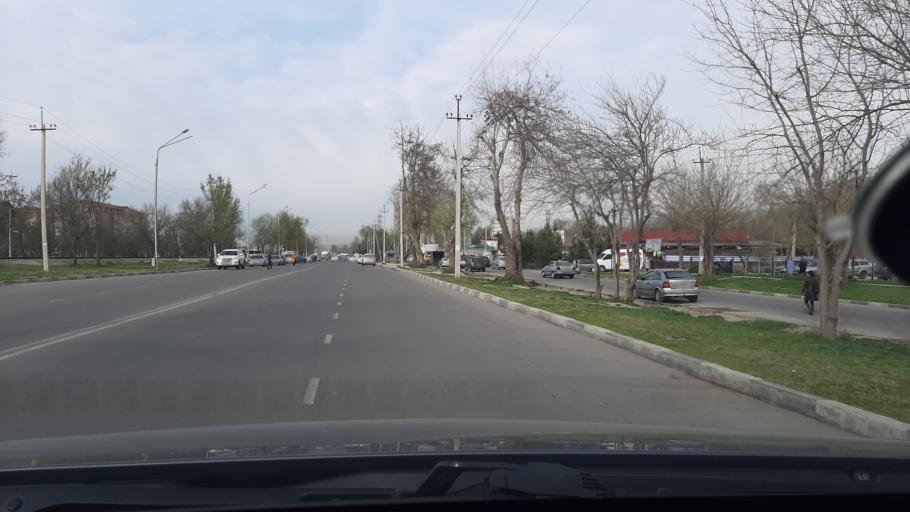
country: TJ
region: Dushanbe
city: Dushanbe
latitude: 38.5687
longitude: 68.7465
